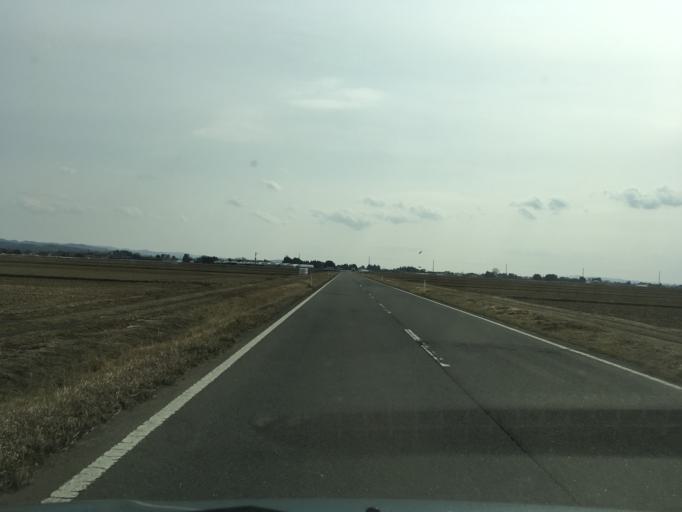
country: JP
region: Iwate
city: Ichinoseki
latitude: 38.7326
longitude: 141.2392
